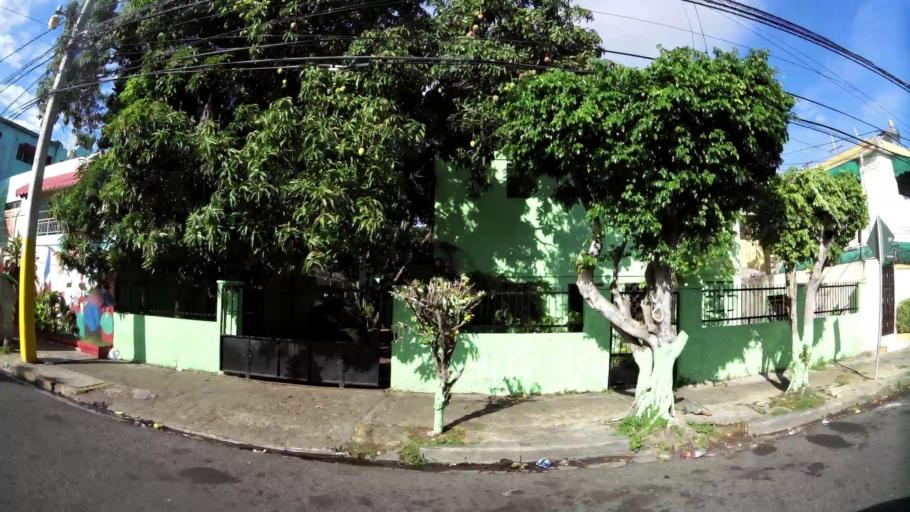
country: DO
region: Santo Domingo
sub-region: Santo Domingo
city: Santo Domingo Este
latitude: 18.4878
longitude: -69.8573
